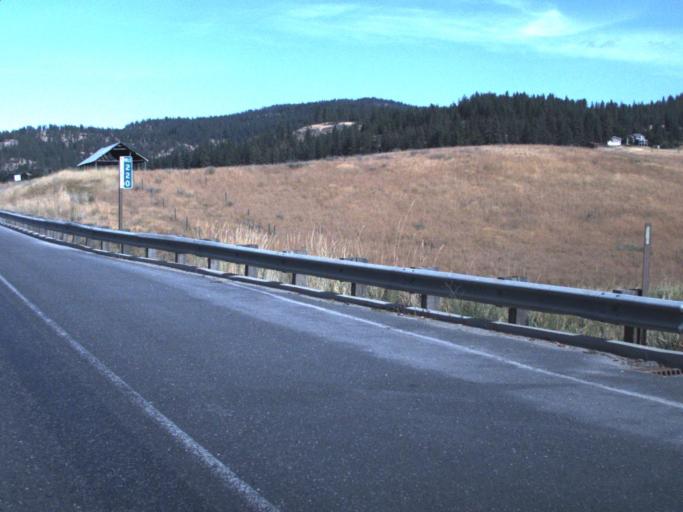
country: US
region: Washington
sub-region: Stevens County
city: Colville
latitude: 48.4159
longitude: -117.8519
